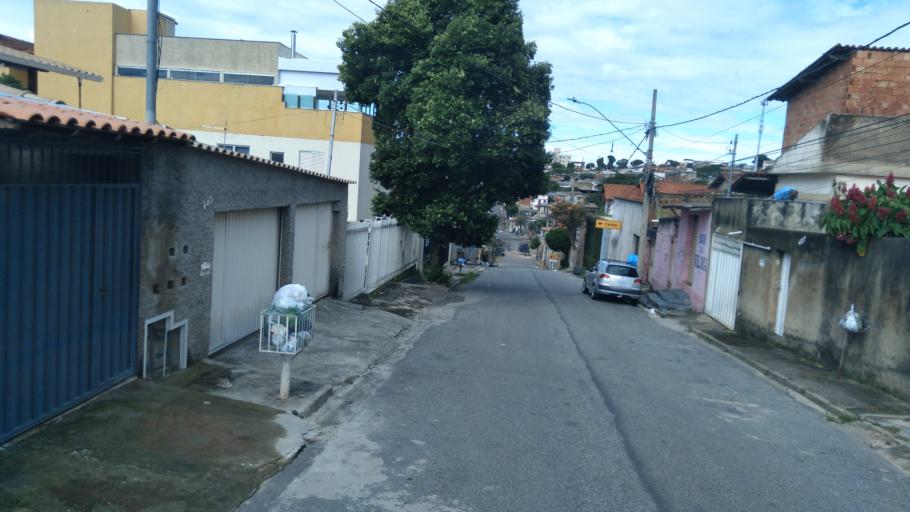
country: BR
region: Minas Gerais
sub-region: Belo Horizonte
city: Belo Horizonte
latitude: -19.9016
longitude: -43.8923
